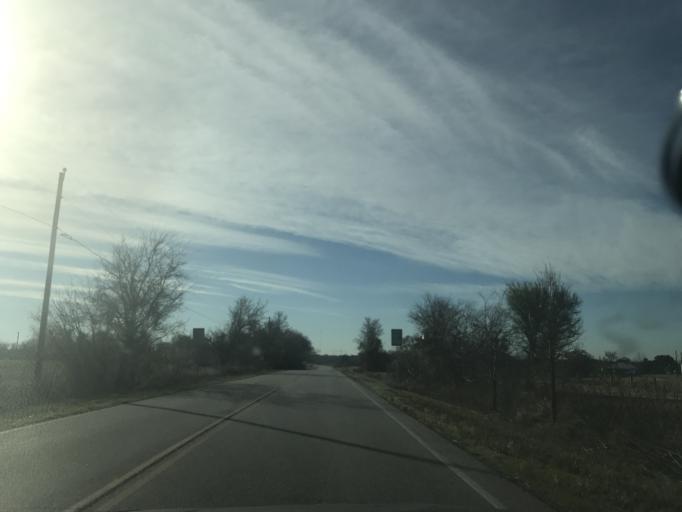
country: US
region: Texas
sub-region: Travis County
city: Manor
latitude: 30.2914
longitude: -97.5230
